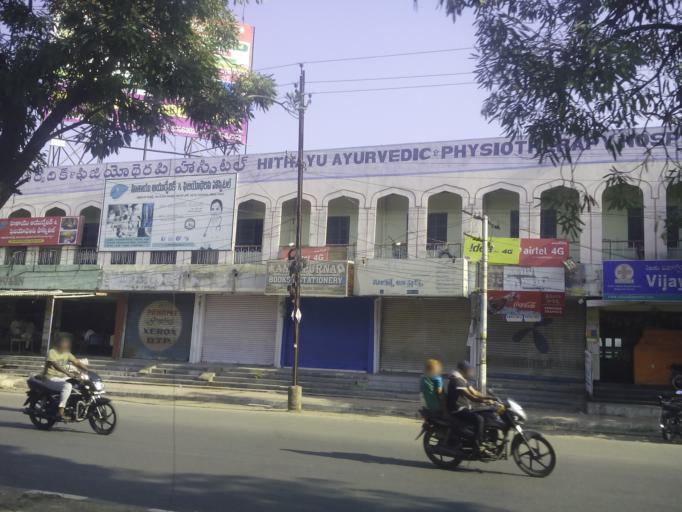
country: IN
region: Telangana
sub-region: Warangal
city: Warangal
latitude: 17.9909
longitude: 79.5940
